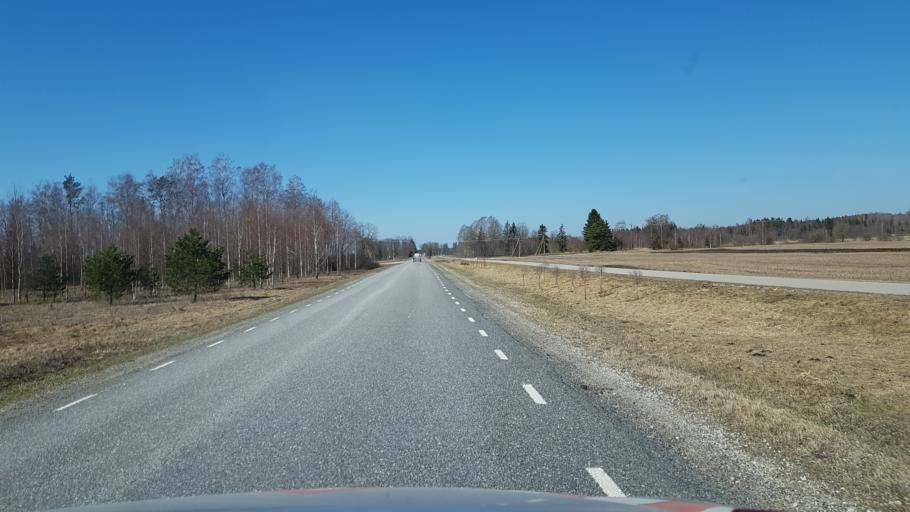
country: EE
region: Laeaene-Virumaa
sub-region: Rakke vald
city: Rakke
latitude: 58.9959
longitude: 26.2150
